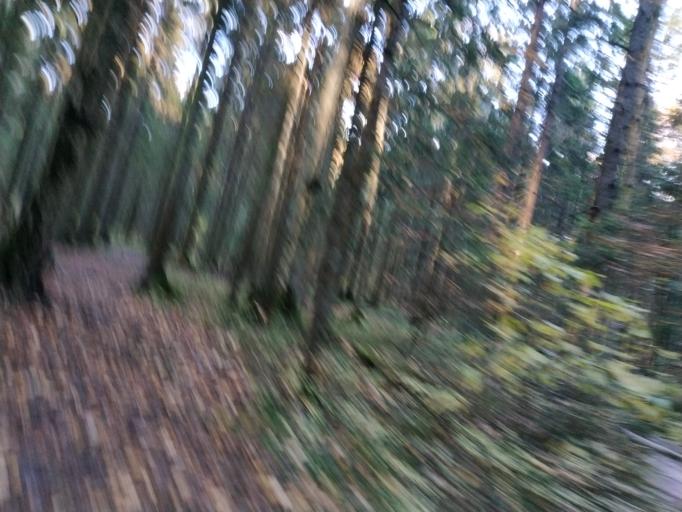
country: RU
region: Moskovskaya
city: Lobnya
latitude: 55.9941
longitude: 37.4692
